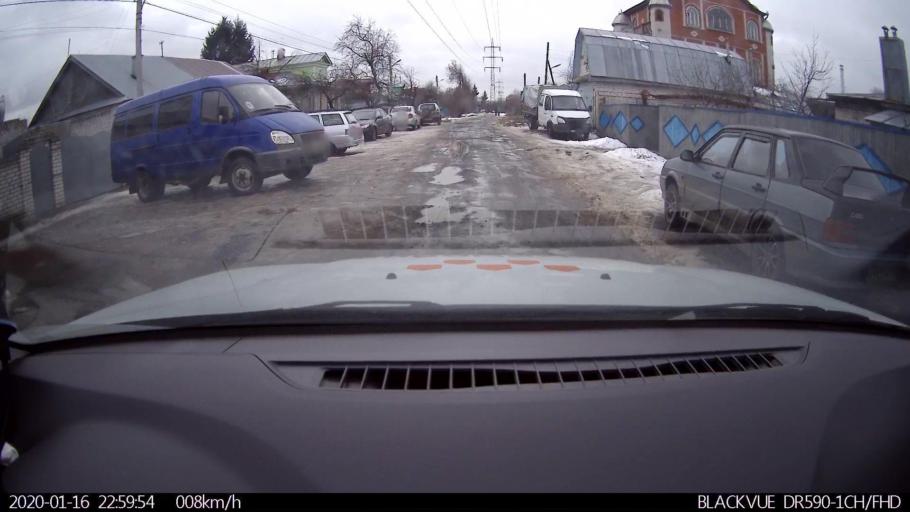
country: RU
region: Nizjnij Novgorod
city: Nizhniy Novgorod
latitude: 56.2866
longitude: 43.9065
